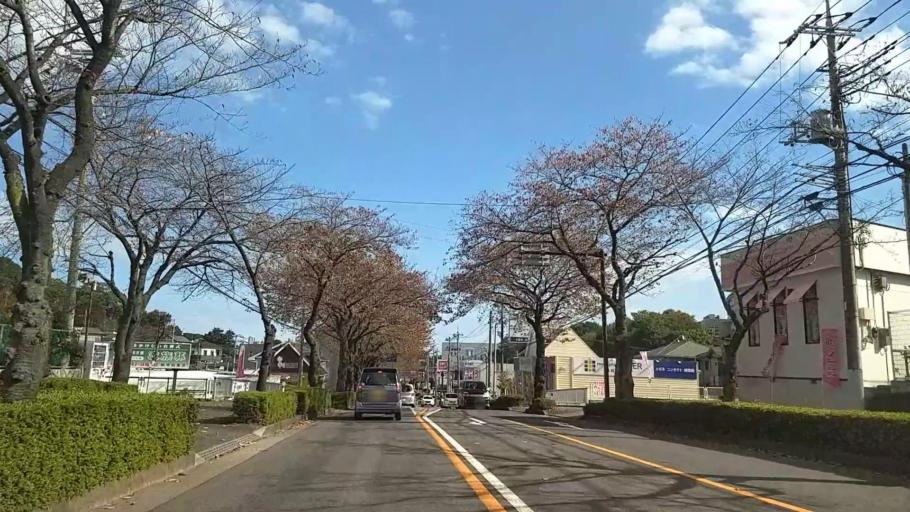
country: JP
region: Kanagawa
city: Hadano
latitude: 35.3620
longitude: 139.2275
